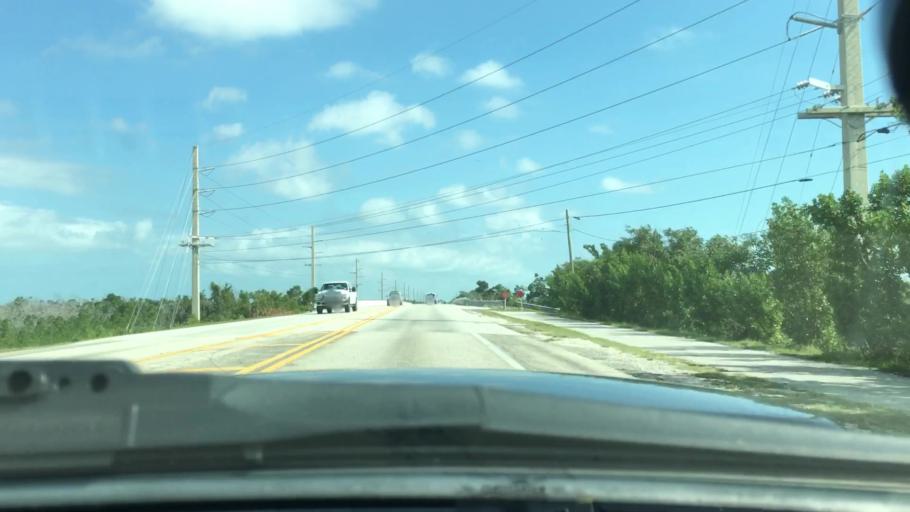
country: US
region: Florida
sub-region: Monroe County
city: Big Pine Key
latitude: 24.6626
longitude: -81.4047
